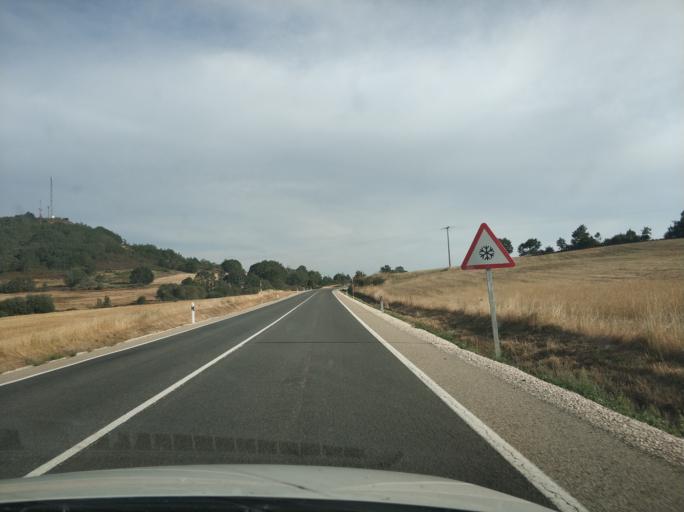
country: ES
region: Castille and Leon
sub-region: Provincia de Burgos
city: Basconcillos del Tozo
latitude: 42.6913
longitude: -3.9777
